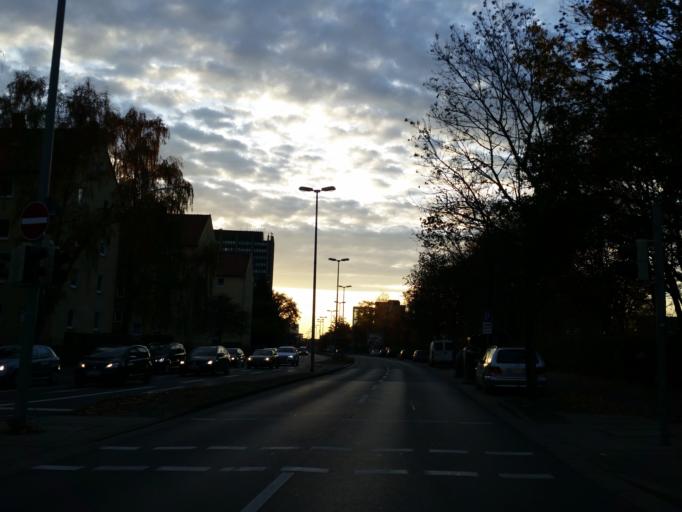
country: DE
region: Lower Saxony
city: Braunschweig
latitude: 52.2777
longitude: 10.5453
